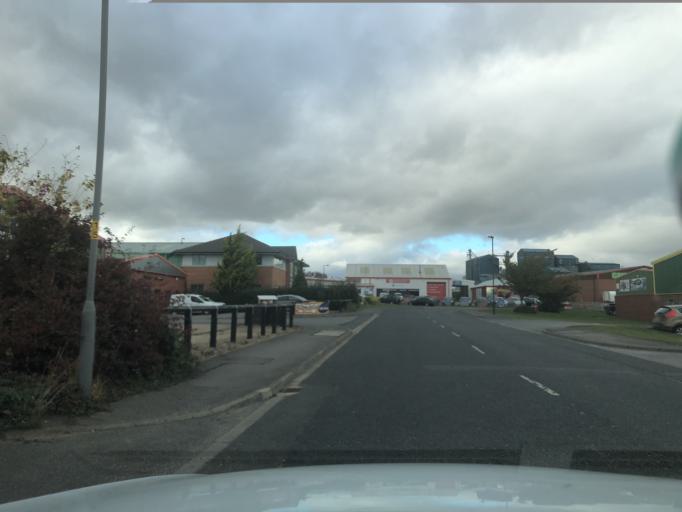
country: GB
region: England
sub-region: North Yorkshire
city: Northallerton
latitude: 54.3491
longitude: -1.4492
